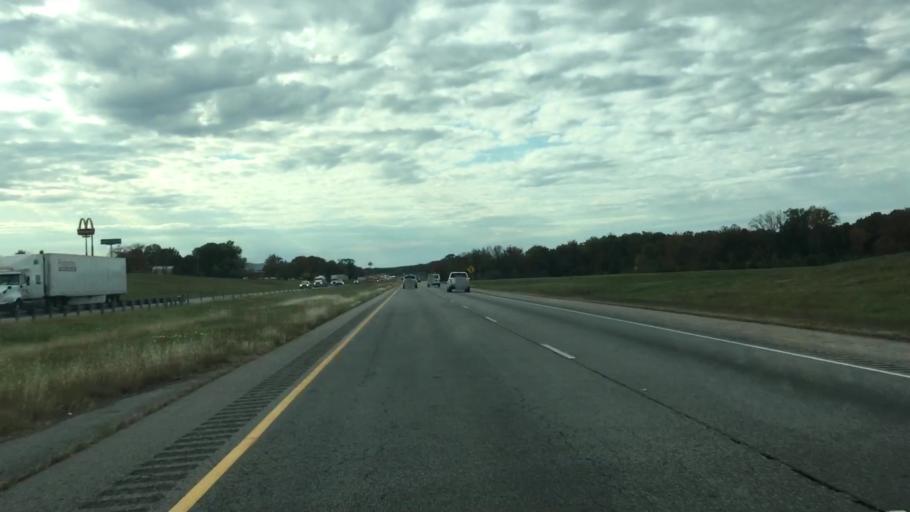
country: US
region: Arkansas
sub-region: Conway County
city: Morrilton
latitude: 35.1743
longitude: -92.7185
